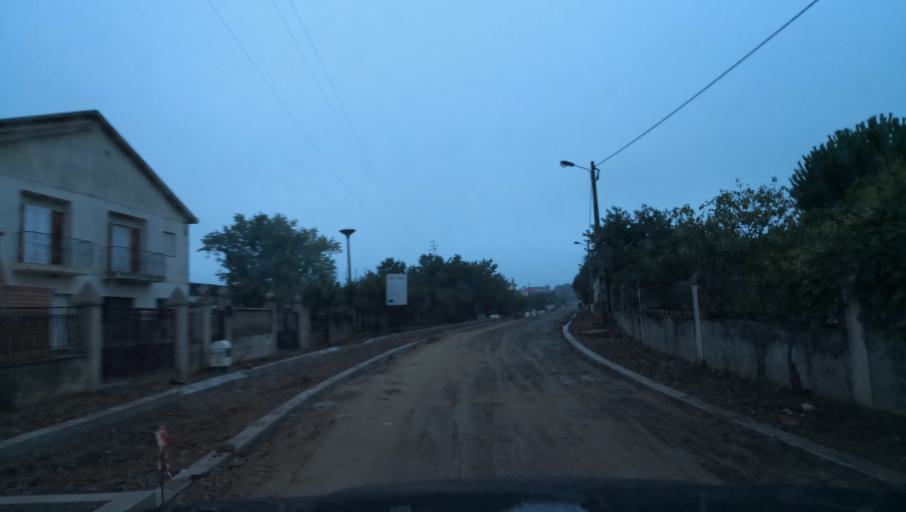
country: PT
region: Vila Real
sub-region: Sabrosa
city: Sabrosa
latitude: 41.2642
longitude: -7.6118
